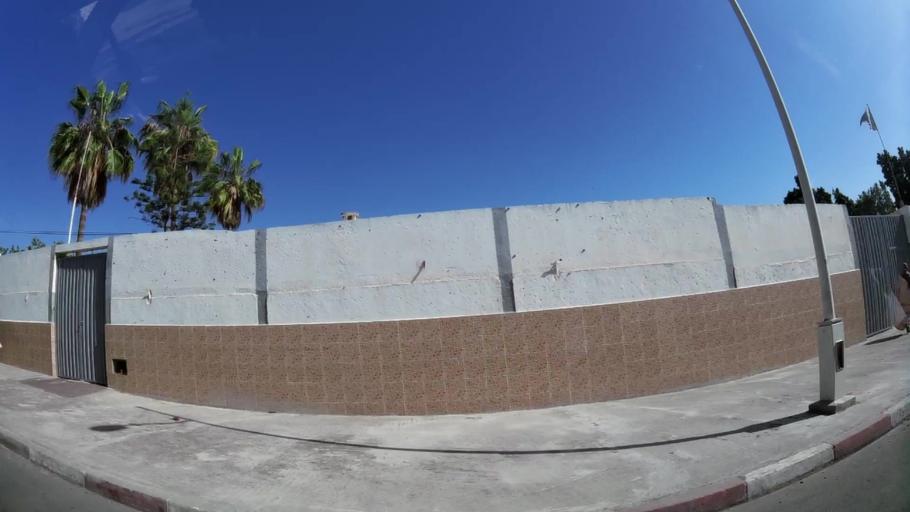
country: MA
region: Souss-Massa-Draa
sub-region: Agadir-Ida-ou-Tnan
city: Agadir
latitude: 30.4109
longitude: -9.5842
